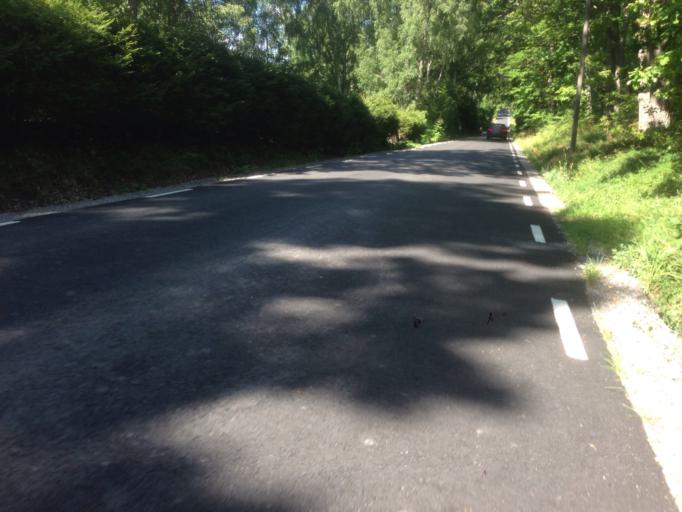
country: SE
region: Stockholm
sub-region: Vaxholms Kommun
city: Vaxholm
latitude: 59.3803
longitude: 18.3757
